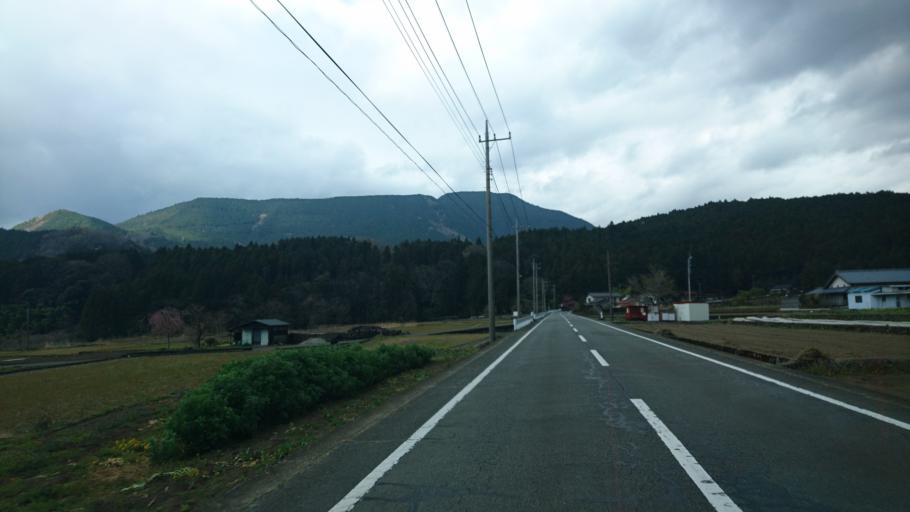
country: JP
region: Shizuoka
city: Fujinomiya
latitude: 35.2870
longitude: 138.5761
